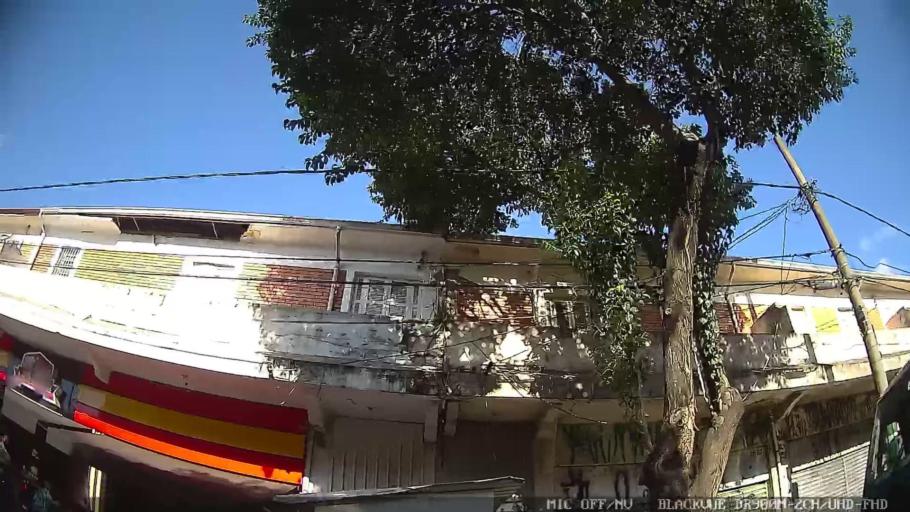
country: BR
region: Sao Paulo
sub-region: Sao Caetano Do Sul
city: Sao Caetano do Sul
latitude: -23.6015
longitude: -46.6016
